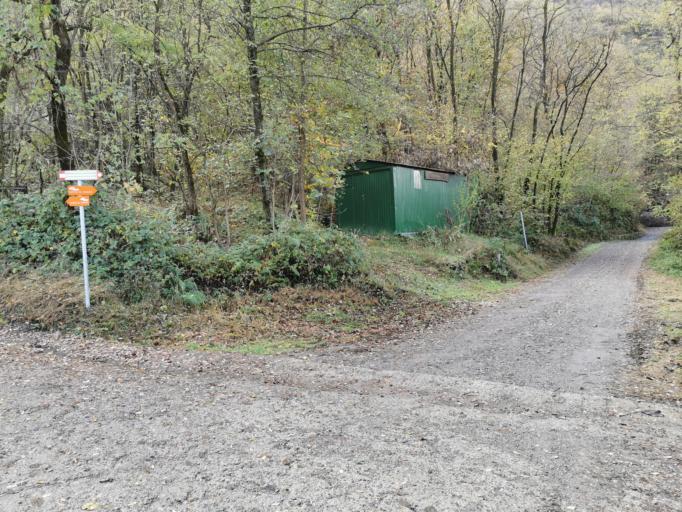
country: IT
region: Lombardy
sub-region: Provincia di Sondrio
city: Piantedo
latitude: 46.1310
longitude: 9.4299
